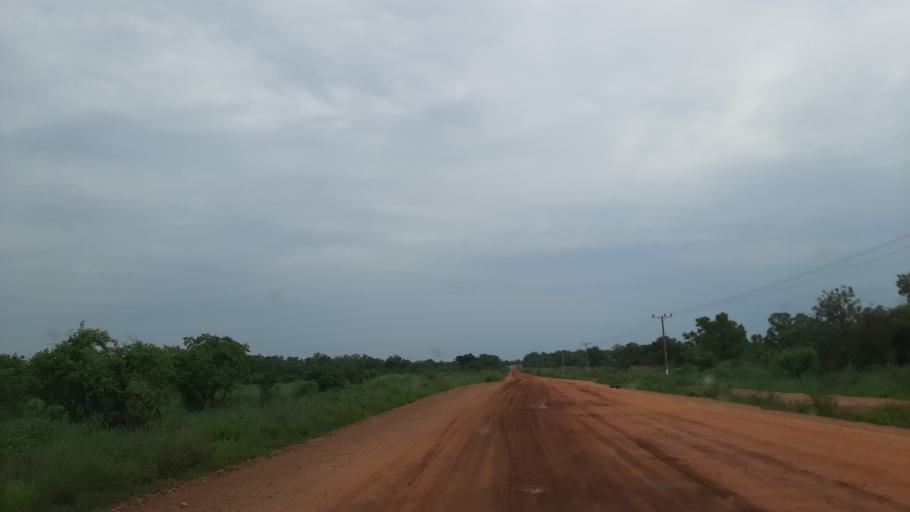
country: ET
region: Gambela
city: Gambela
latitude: 8.1453
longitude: 34.3019
